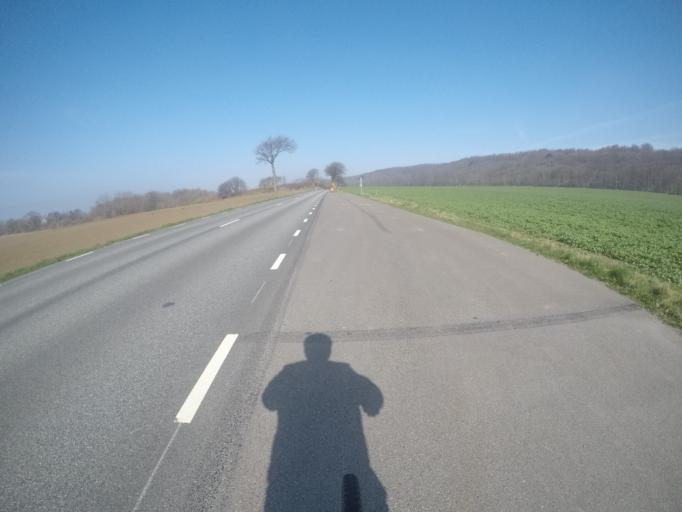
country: SE
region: Skane
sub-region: Hoganas Kommun
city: Hoganas
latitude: 56.2752
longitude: 12.5158
